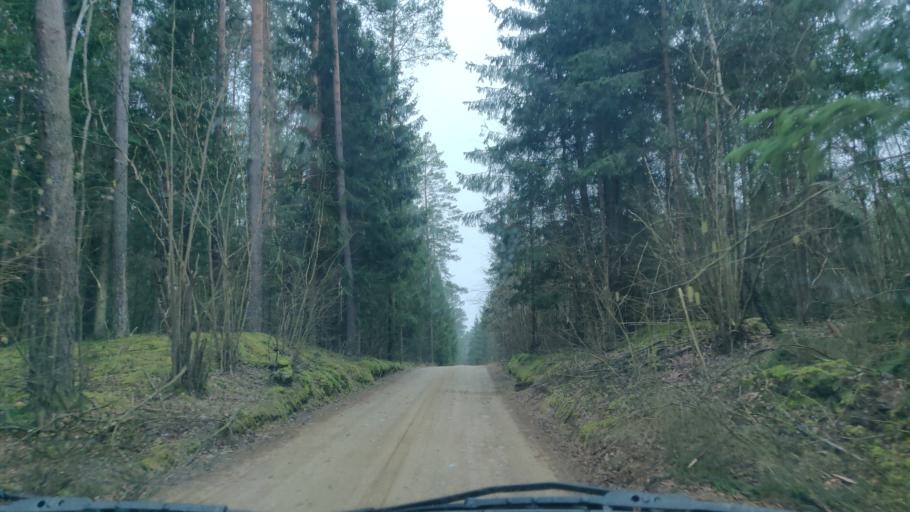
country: LT
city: Trakai
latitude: 54.5661
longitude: 24.9645
